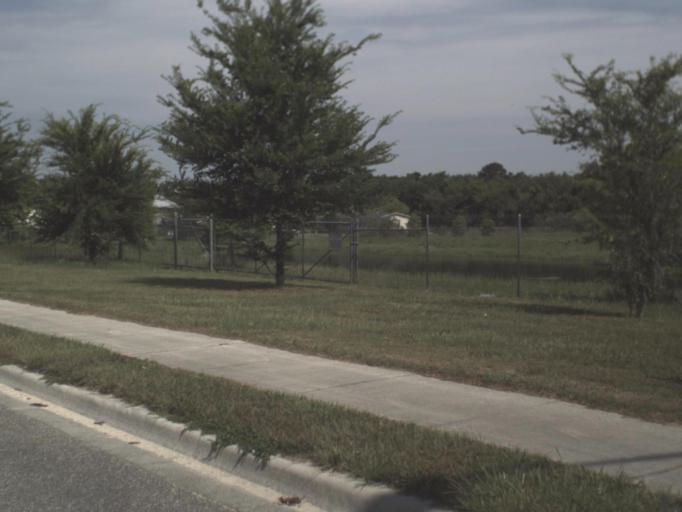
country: US
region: Florida
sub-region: Putnam County
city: East Palatka
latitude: 29.7145
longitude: -81.5004
